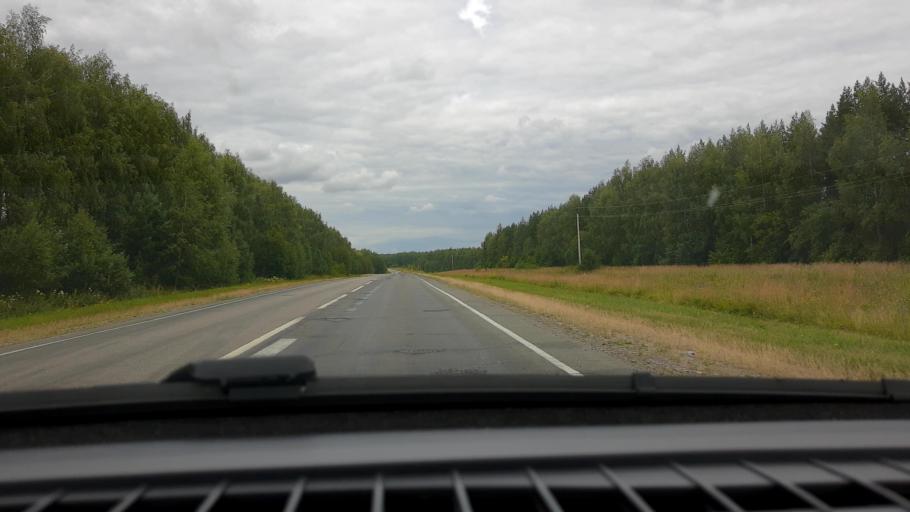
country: RU
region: Nizjnij Novgorod
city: Knyaginino
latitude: 55.7148
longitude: 45.2043
